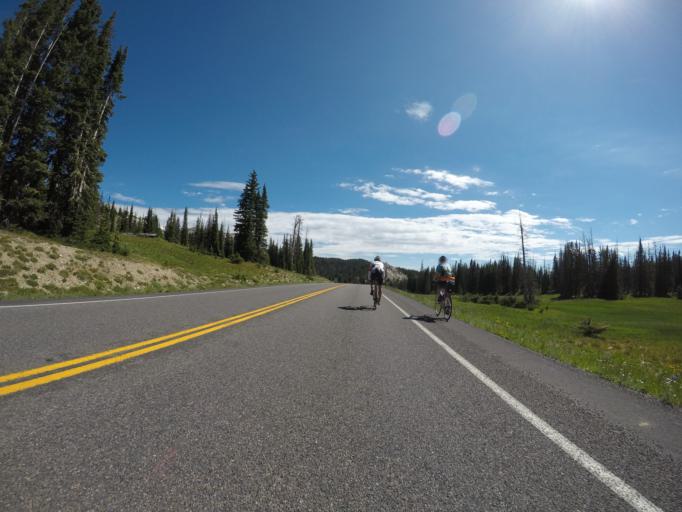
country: US
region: Wyoming
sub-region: Carbon County
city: Saratoga
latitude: 41.3201
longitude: -106.3432
